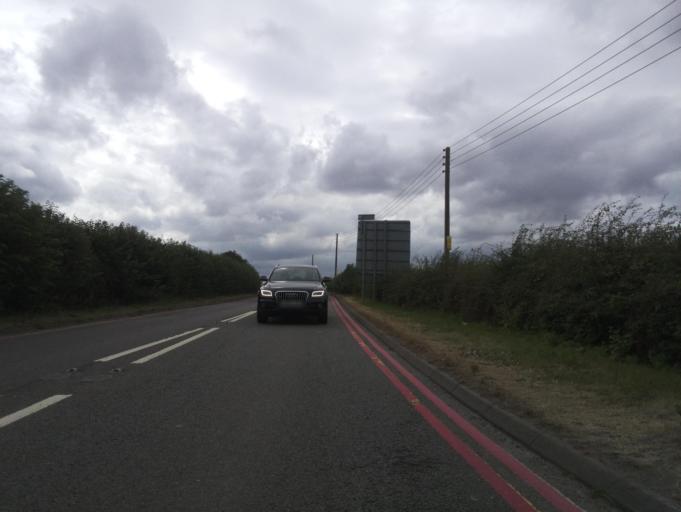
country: GB
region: England
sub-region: Leicestershire
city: Castle Donington
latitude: 52.8244
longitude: -1.3649
